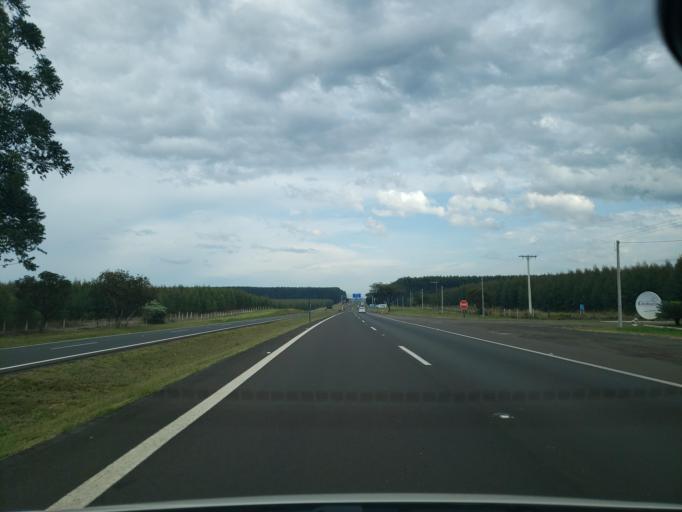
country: BR
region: Sao Paulo
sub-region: Itirapina
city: Itirapina
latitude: -22.2604
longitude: -47.8803
